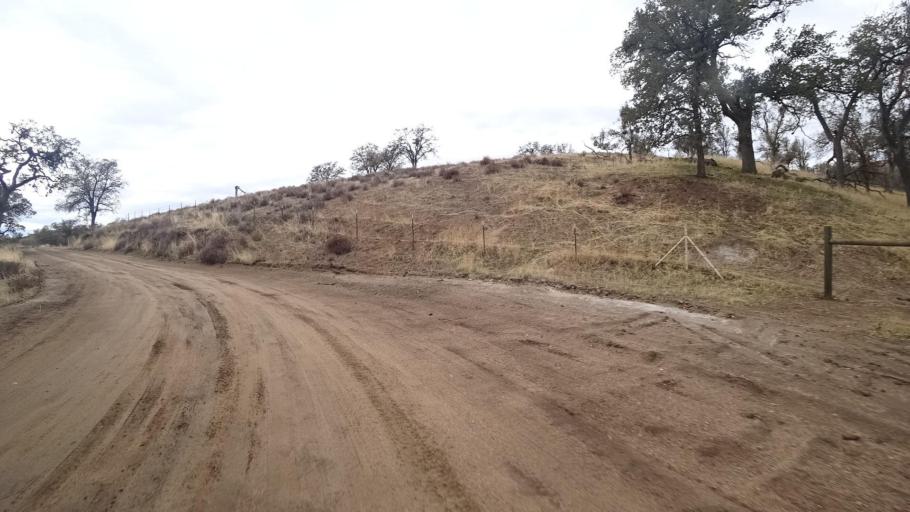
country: US
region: California
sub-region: Kern County
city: Stallion Springs
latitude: 35.1171
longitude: -118.6949
